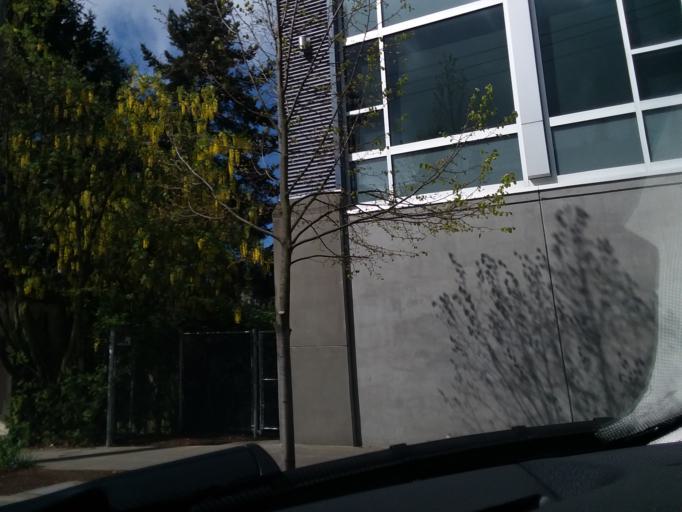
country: US
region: Washington
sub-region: King County
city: Seattle
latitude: 47.6342
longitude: -122.3255
